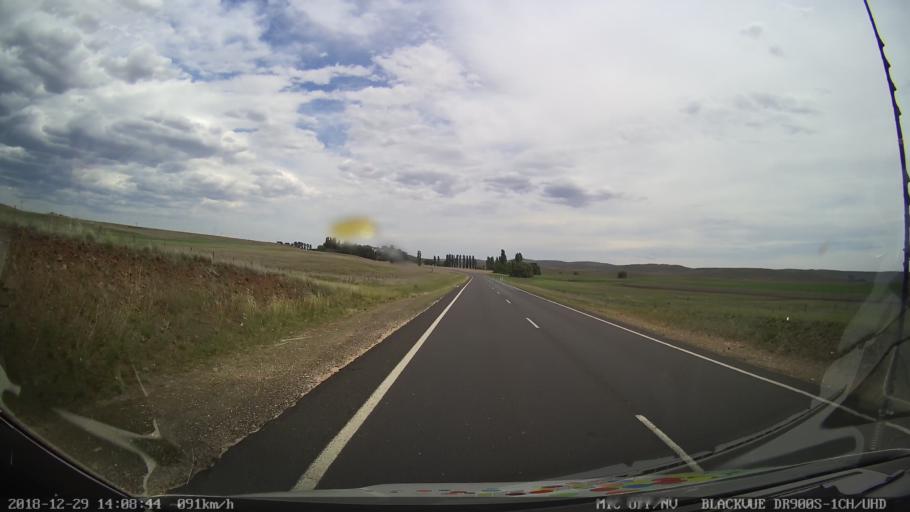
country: AU
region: New South Wales
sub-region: Cooma-Monaro
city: Cooma
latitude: -36.3694
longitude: 149.2137
